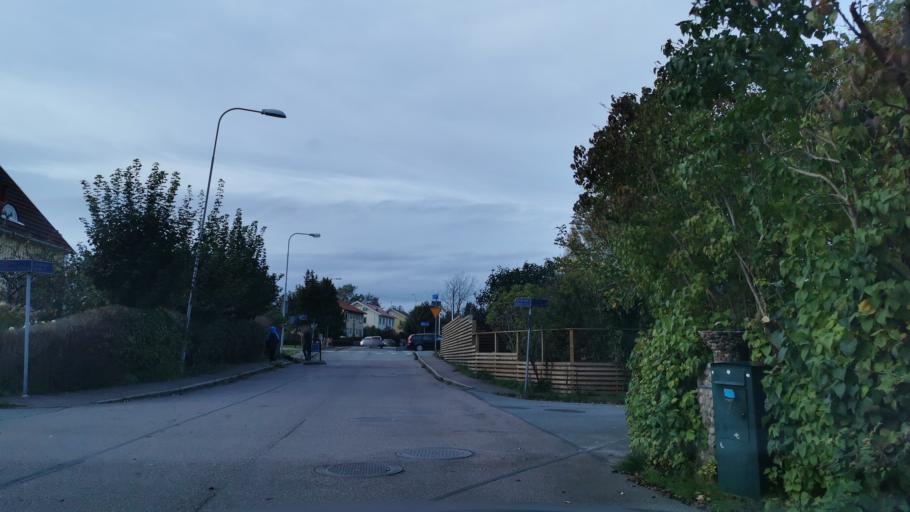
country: SE
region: Vaestra Goetaland
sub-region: Goteborg
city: Eriksbo
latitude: 57.7344
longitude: 12.0454
